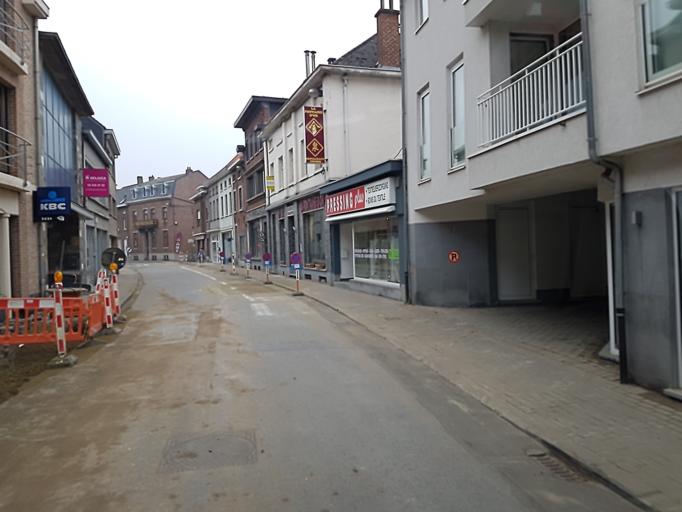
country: BE
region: Flanders
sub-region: Provincie Vlaams-Brabant
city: Sint-Genesius-Rode
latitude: 50.7448
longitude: 4.3444
